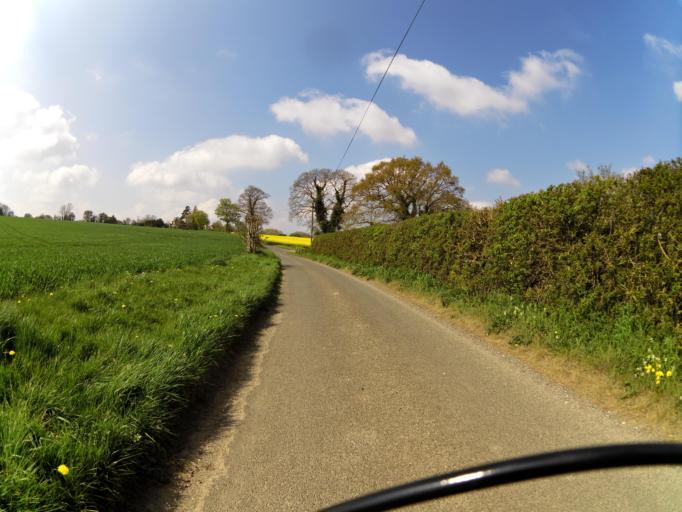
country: GB
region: England
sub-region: Suffolk
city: Hadleigh
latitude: 52.0811
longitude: 1.0138
